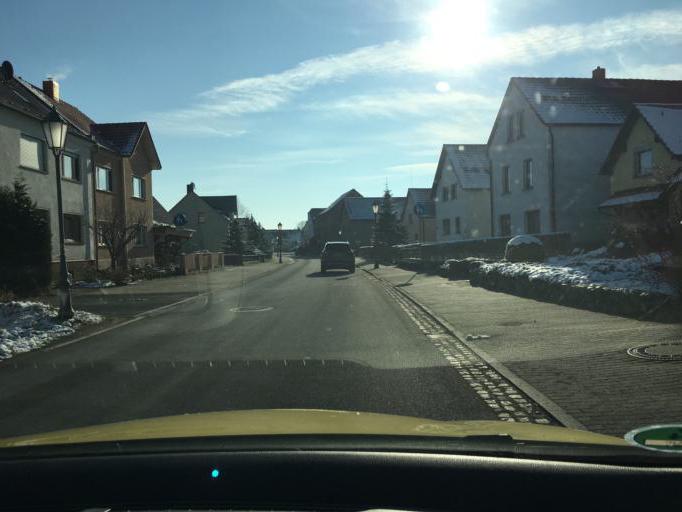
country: DE
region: Saxony
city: Grossposna
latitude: 51.2849
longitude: 12.5286
